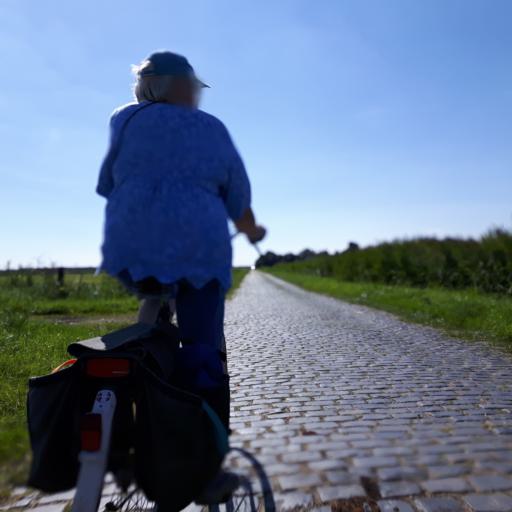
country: NL
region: North Brabant
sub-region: Gemeente Woensdrecht
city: Woensdrecht
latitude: 51.4370
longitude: 4.2754
